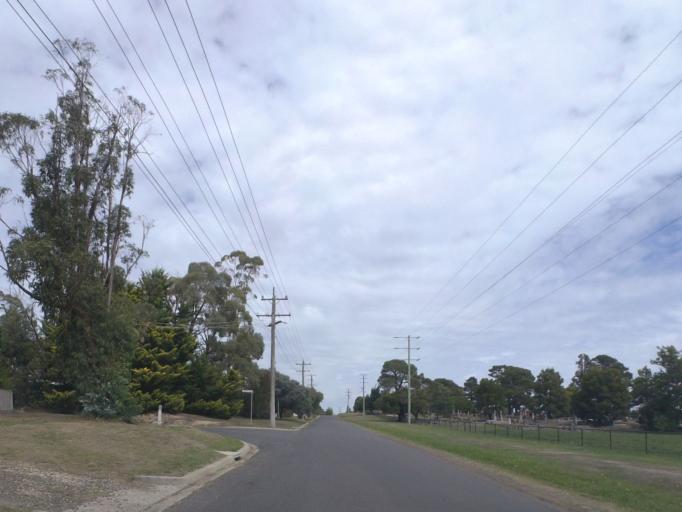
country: AU
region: Victoria
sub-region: Hume
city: Sunbury
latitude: -37.3522
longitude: 144.5363
